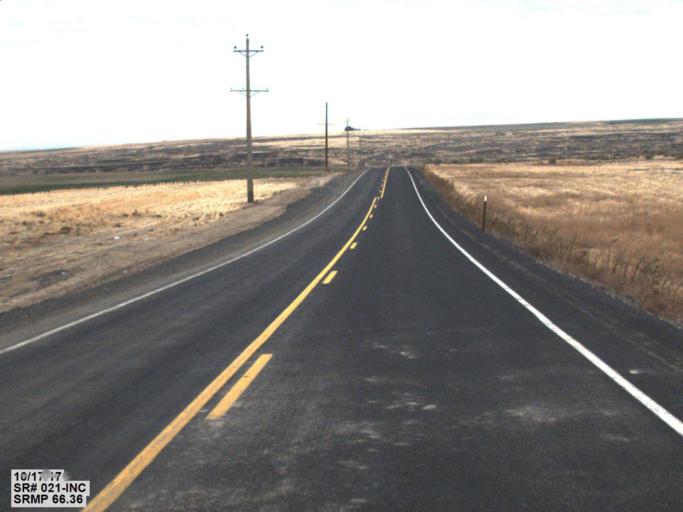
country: US
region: Washington
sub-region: Adams County
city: Ritzville
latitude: 47.4559
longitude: -118.7518
